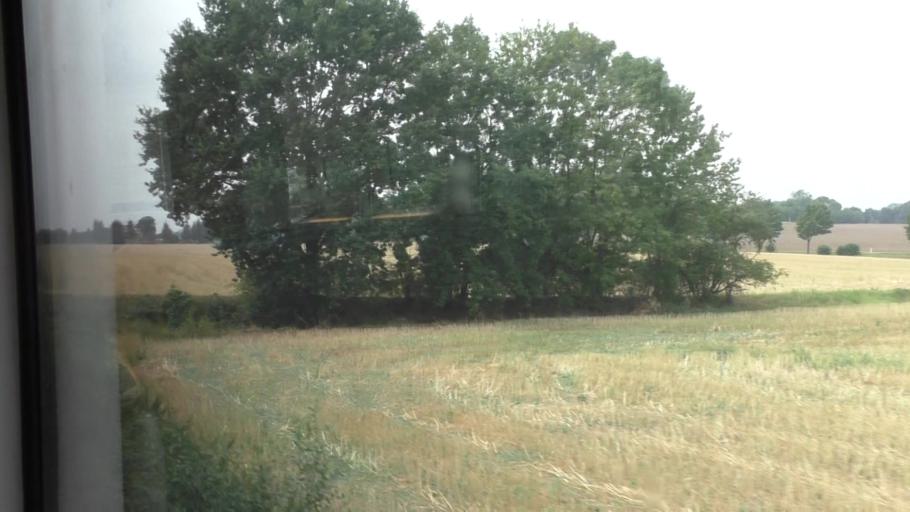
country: DE
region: Saxony
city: Hirschfelde
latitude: 50.9200
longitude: 14.8559
